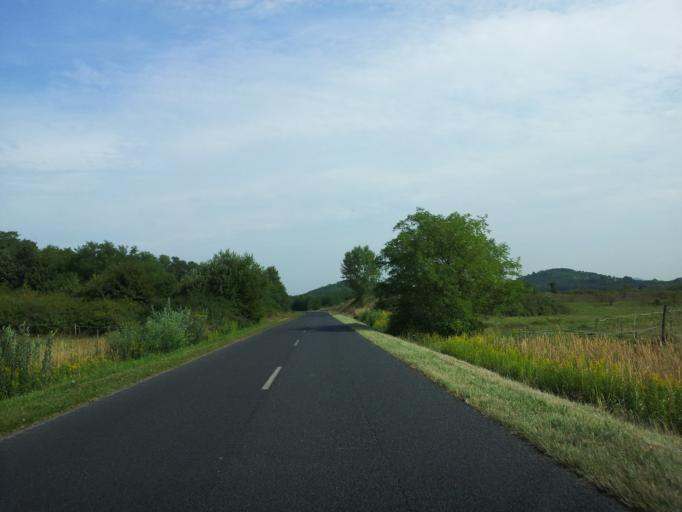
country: HU
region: Veszprem
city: Badacsonytomaj
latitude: 46.8439
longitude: 17.5514
